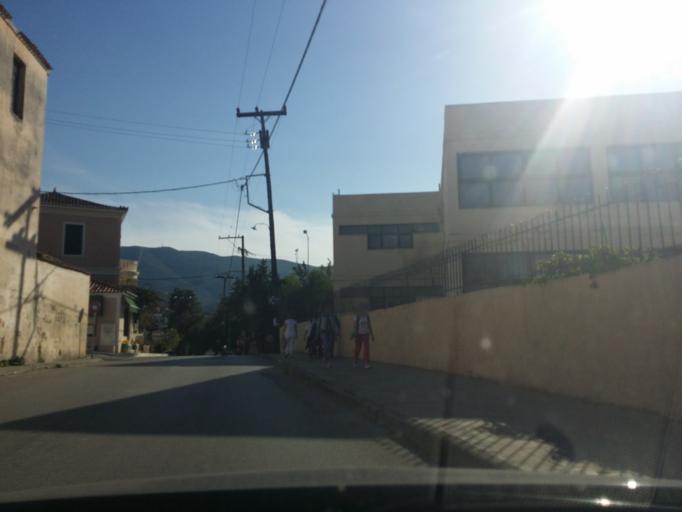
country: GR
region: Attica
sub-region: Nomos Piraios
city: Poros
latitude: 37.5043
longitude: 23.4565
